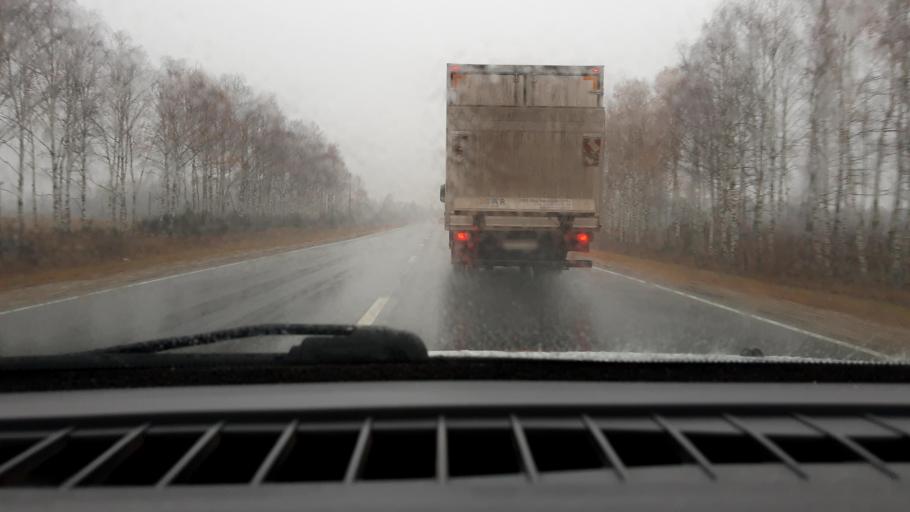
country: RU
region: Nizjnij Novgorod
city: Linda
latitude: 56.5737
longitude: 44.0232
